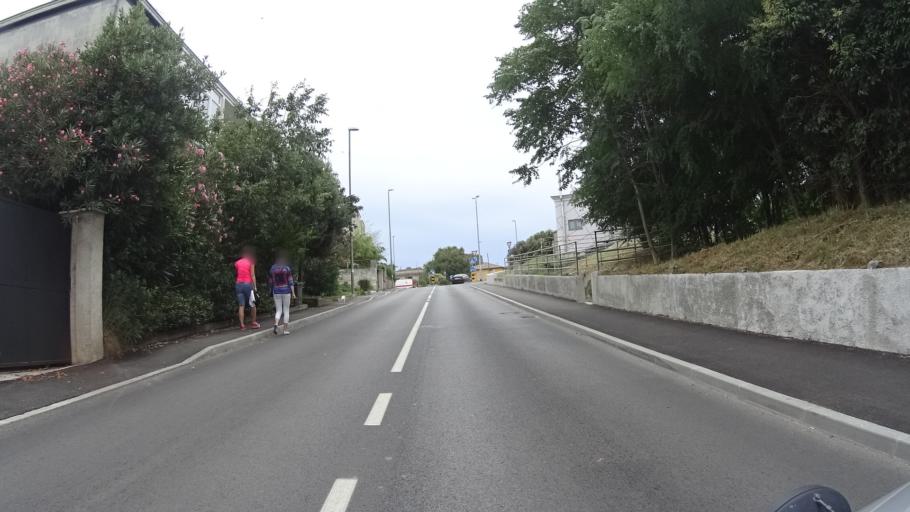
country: HR
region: Istarska
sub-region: Grad Pula
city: Pula
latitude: 44.8589
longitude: 13.8449
